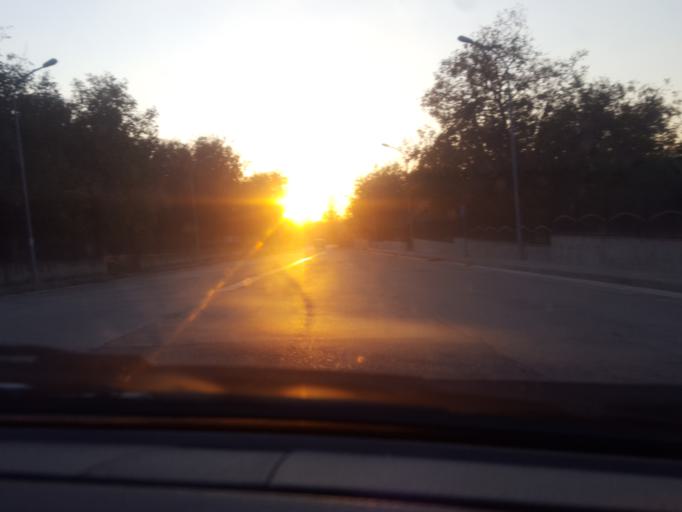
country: IT
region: Campania
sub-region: Provincia di Caserta
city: Arienzo
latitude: 41.0278
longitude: 14.5050
